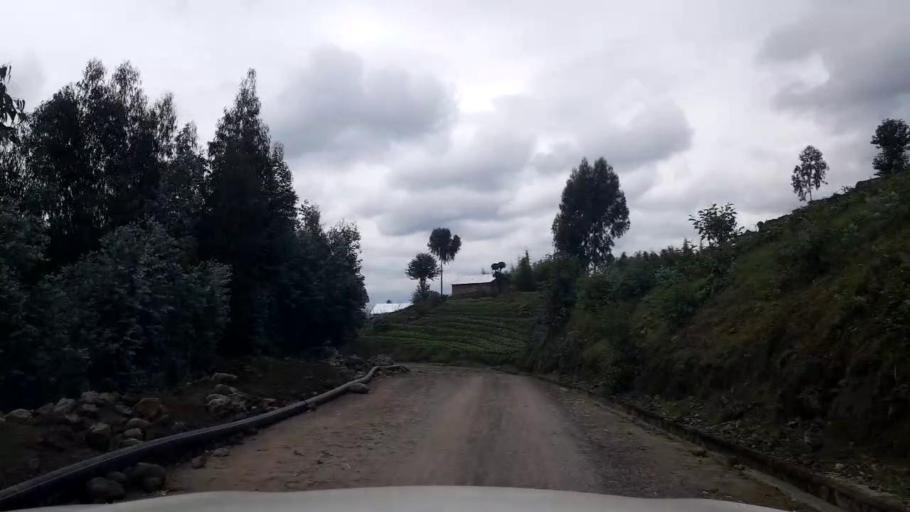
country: RW
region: Northern Province
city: Musanze
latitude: -1.5353
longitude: 29.5332
